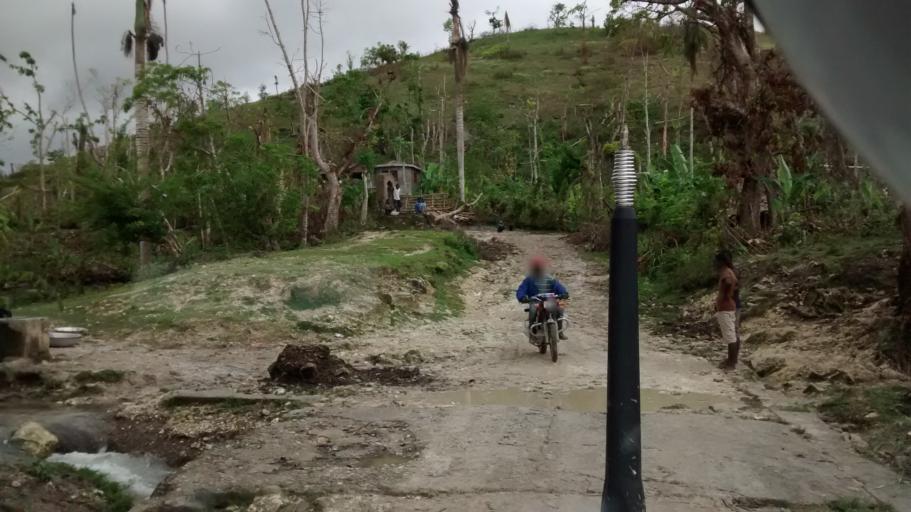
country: HT
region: Grandans
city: Jeremie
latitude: 18.5635
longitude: -74.1525
